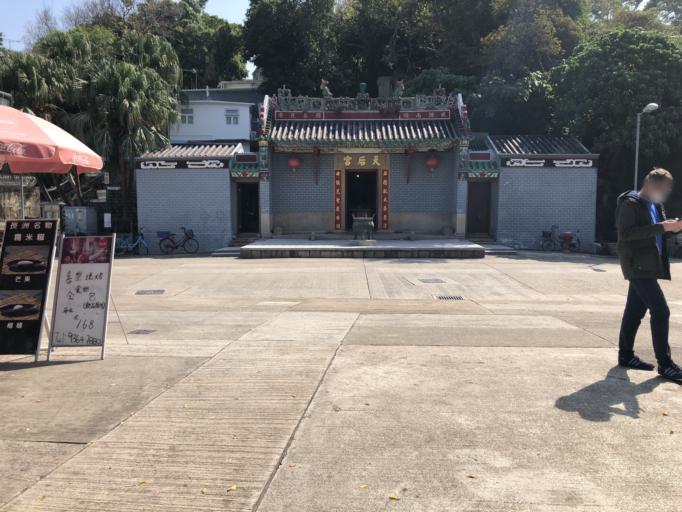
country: HK
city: Yung Shue Wan
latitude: 22.2050
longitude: 114.0271
